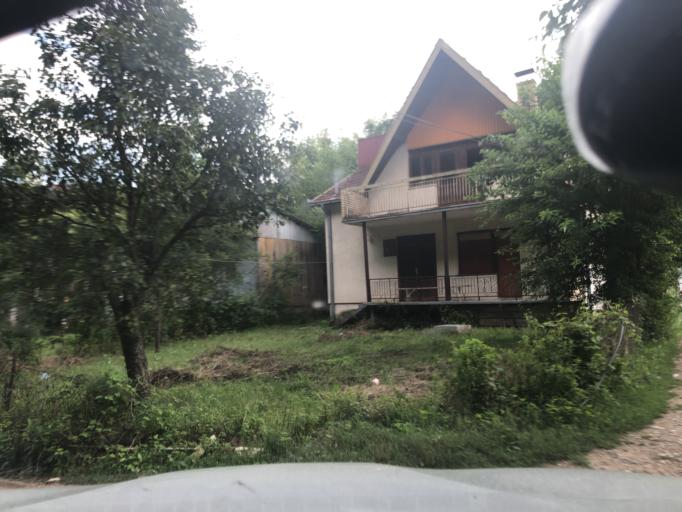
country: RS
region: Central Serbia
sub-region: Jablanicki Okrug
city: Medvega
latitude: 42.7878
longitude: 21.5858
